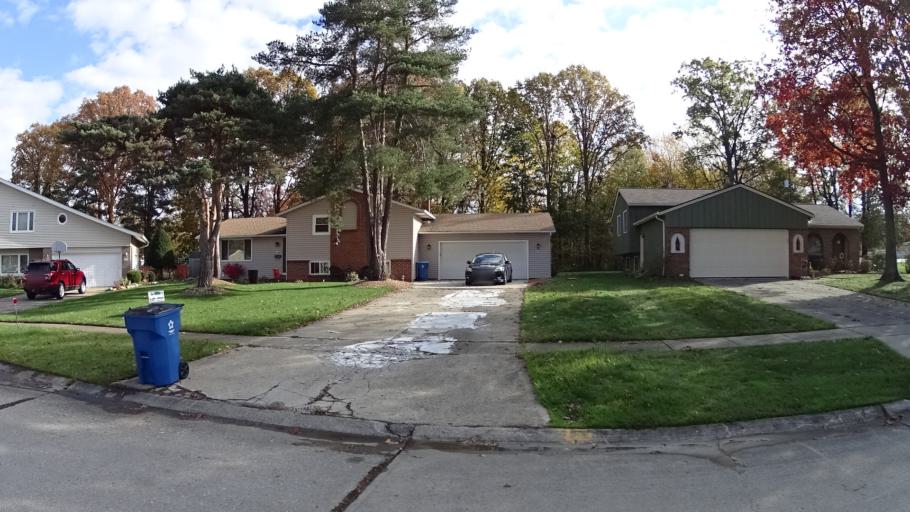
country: US
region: Ohio
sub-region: Lorain County
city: Lorain
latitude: 41.4226
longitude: -82.1886
